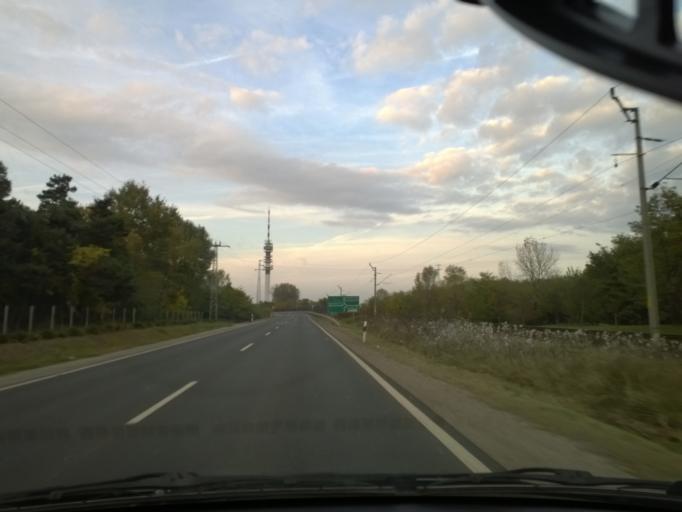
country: HU
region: Bacs-Kiskun
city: Kiskunfelegyhaza
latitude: 46.6820
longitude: 19.8277
